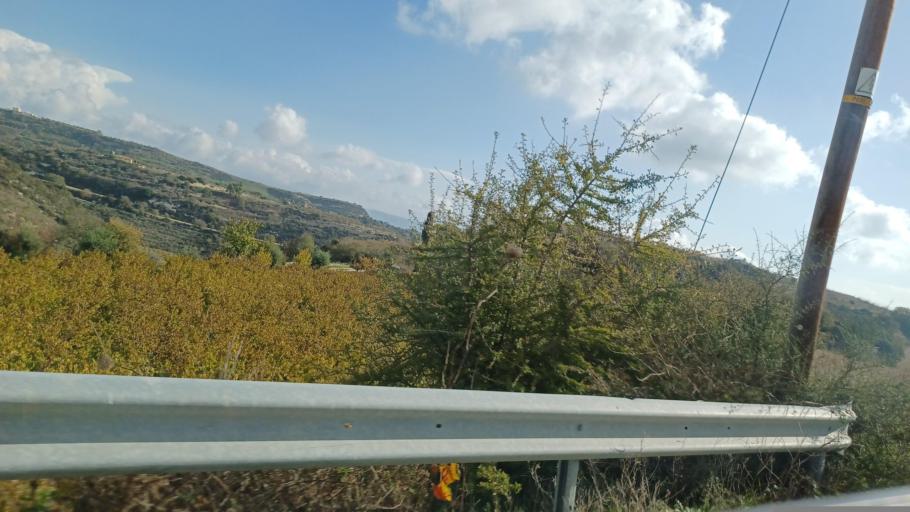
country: CY
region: Pafos
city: Mesogi
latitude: 34.8254
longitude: 32.4803
